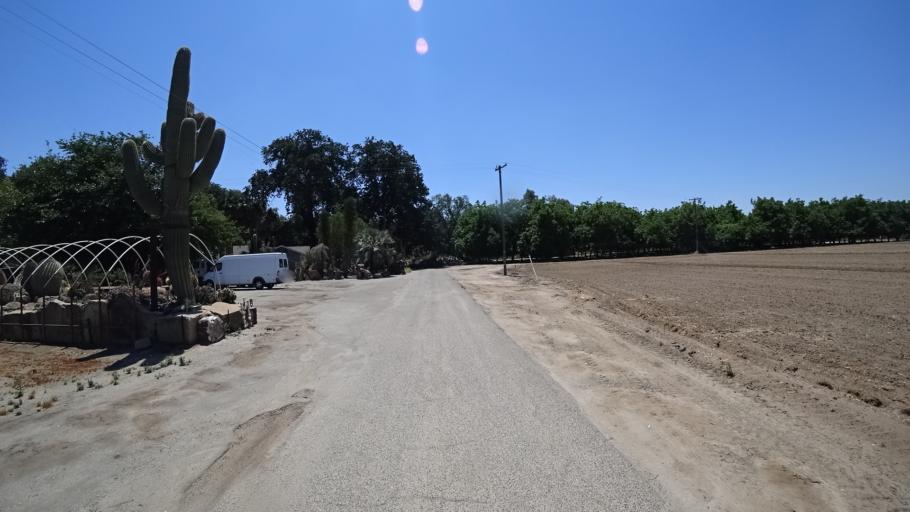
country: US
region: California
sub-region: Kings County
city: Lucerne
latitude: 36.4349
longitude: -119.6095
